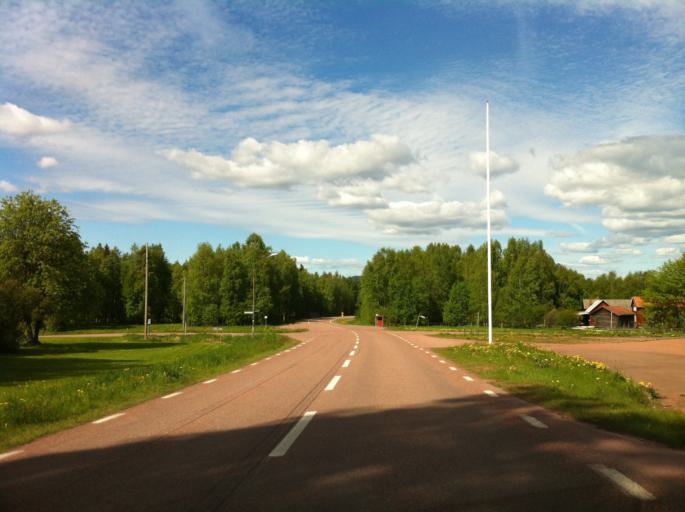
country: SE
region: Dalarna
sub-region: Mora Kommun
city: Mora
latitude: 60.9166
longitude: 14.6097
